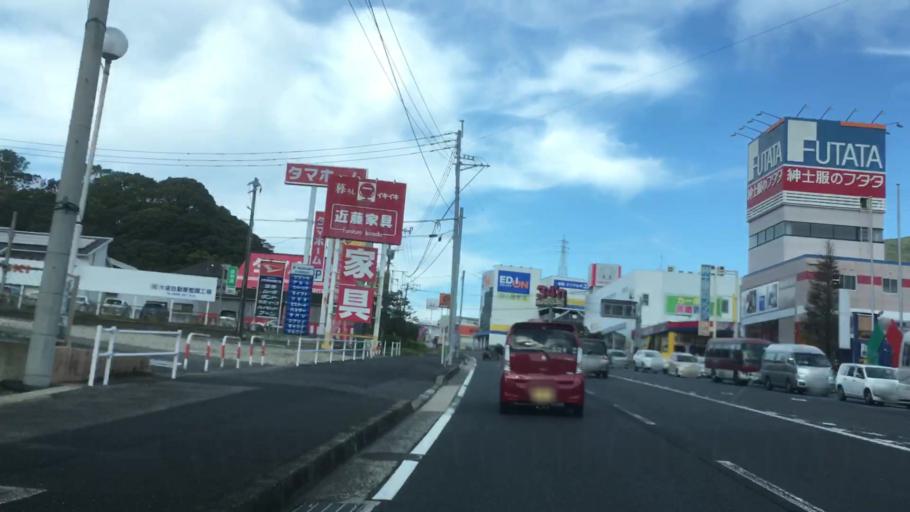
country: JP
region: Nagasaki
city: Sasebo
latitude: 33.1553
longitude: 129.7713
